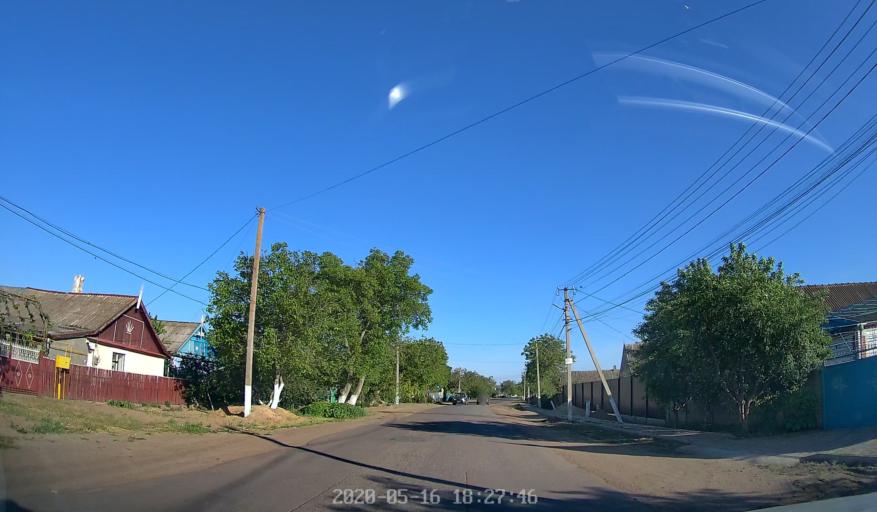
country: MD
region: Telenesti
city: Dnestrovsc
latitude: 46.5450
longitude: 30.0113
